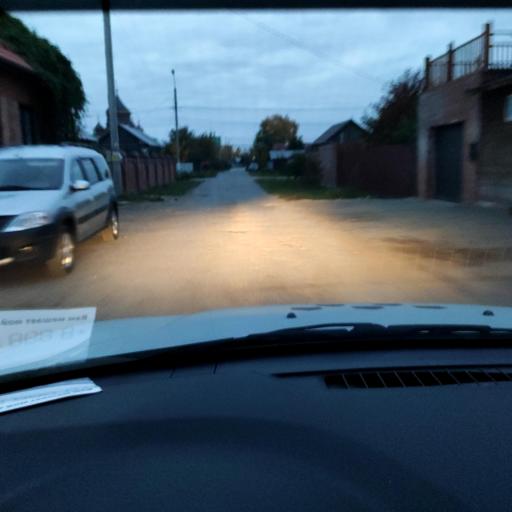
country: RU
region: Samara
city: Tol'yatti
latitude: 53.5260
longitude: 49.4085
